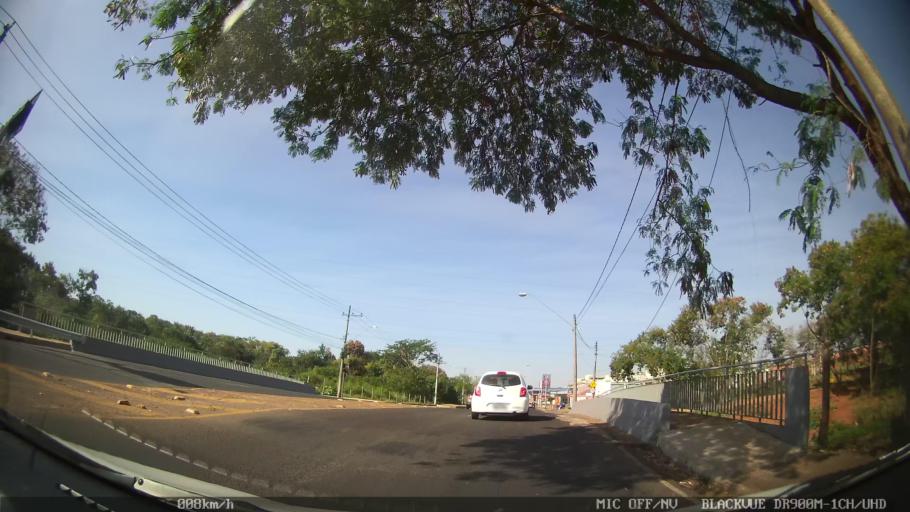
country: BR
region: Sao Paulo
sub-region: Sao Jose Do Rio Preto
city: Sao Jose do Rio Preto
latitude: -20.7835
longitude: -49.3825
